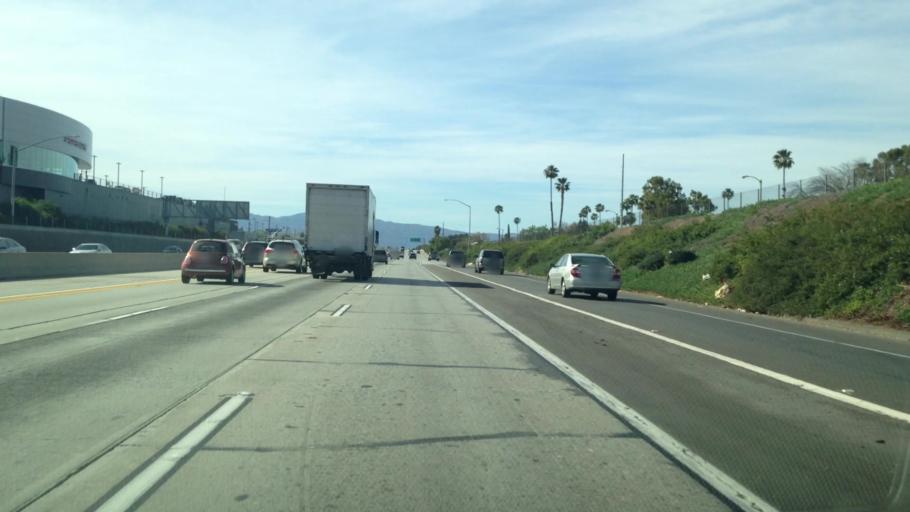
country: US
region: California
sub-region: Riverside County
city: Riverside
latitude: 33.9266
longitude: -117.4214
